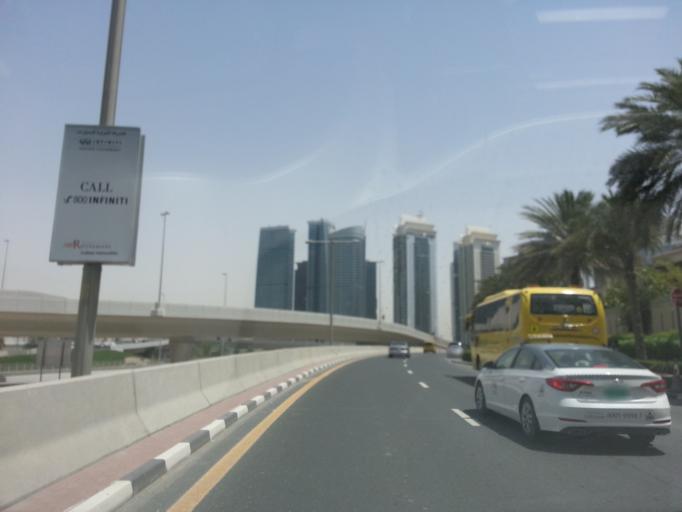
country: AE
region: Dubai
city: Dubai
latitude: 25.0866
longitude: 55.1499
